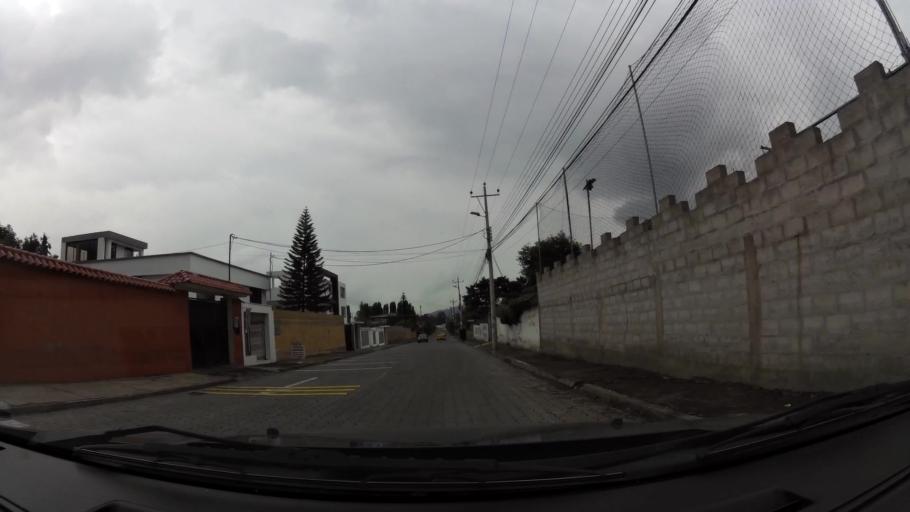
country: EC
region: Pichincha
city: Sangolqui
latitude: -0.3134
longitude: -78.4647
